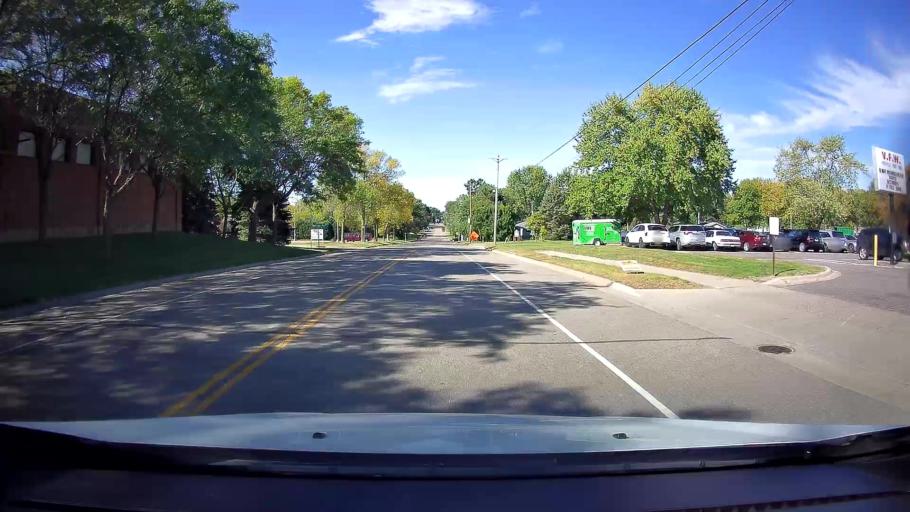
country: US
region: Minnesota
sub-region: Ramsey County
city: Roseville
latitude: 45.0228
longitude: -93.1487
